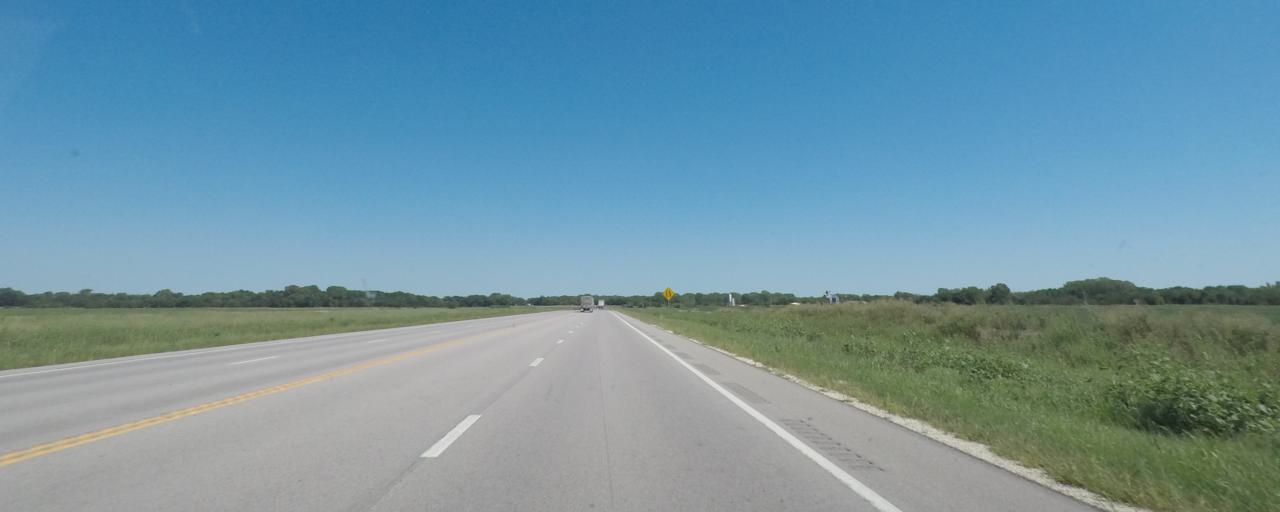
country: US
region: Kansas
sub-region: Chase County
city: Cottonwood Falls
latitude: 38.4050
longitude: -96.4022
